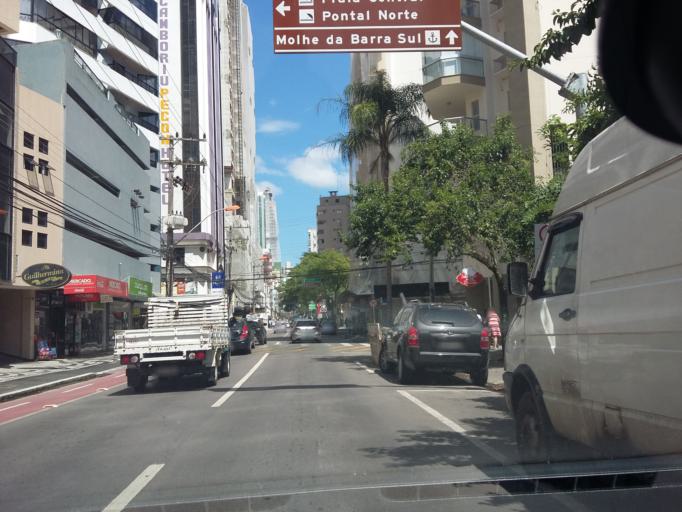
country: BR
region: Santa Catarina
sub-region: Balneario Camboriu
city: Balneario Camboriu
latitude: -26.9780
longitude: -48.6369
